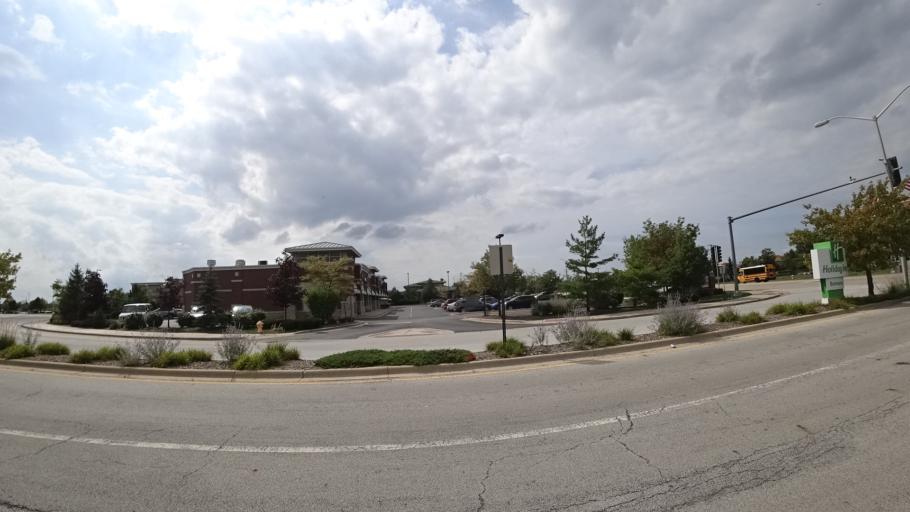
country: US
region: Illinois
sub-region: Cook County
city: Tinley Park
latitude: 41.5581
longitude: -87.7897
